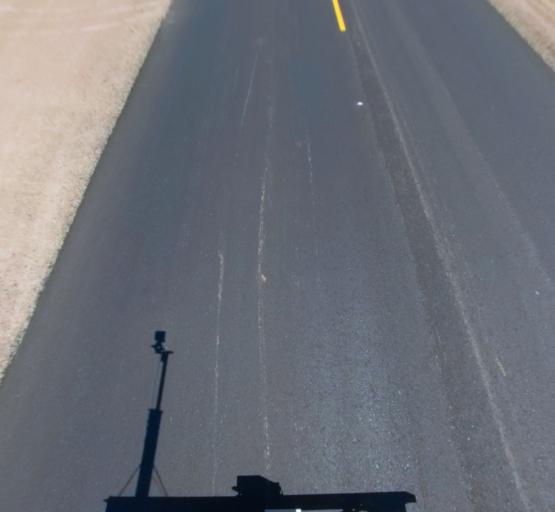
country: US
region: California
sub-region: Madera County
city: Bonadelle Ranchos-Madera Ranchos
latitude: 36.8936
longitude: -119.8574
